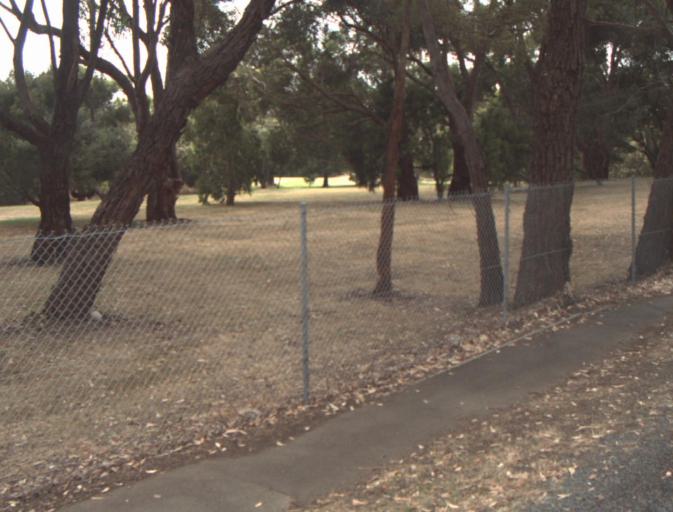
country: AU
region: Tasmania
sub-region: Launceston
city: East Launceston
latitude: -41.4664
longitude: 147.1673
